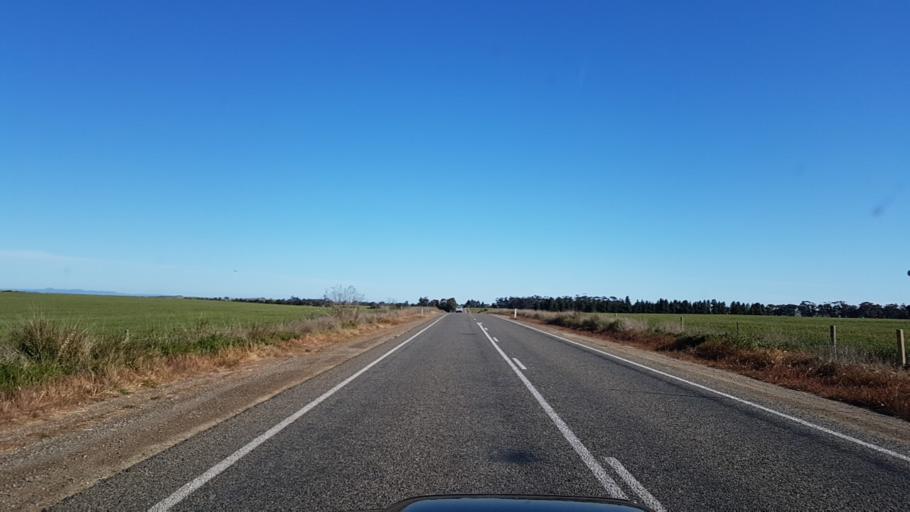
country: AU
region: South Australia
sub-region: Light
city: Kapunda
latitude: -34.2190
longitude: 138.7399
